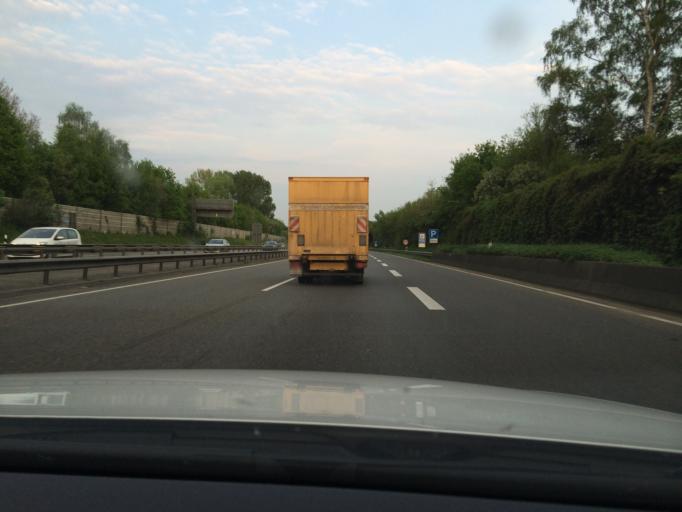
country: DE
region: Lower Saxony
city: Delmenhorst
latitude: 53.0362
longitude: 8.5937
